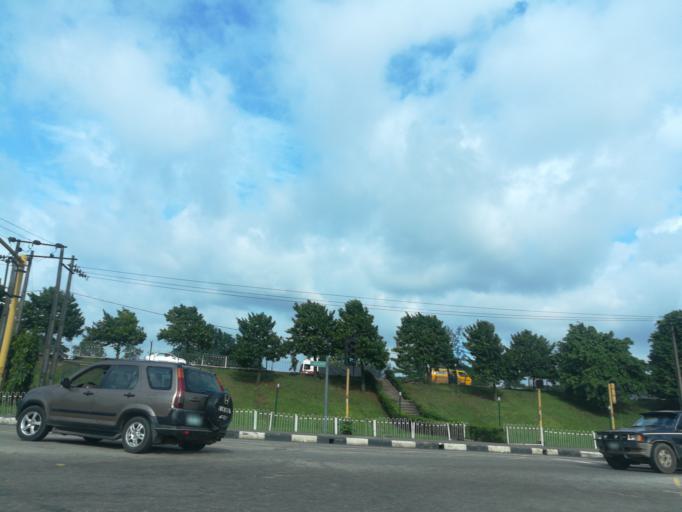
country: NG
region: Lagos
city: Ikeja
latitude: 6.6210
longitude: 3.3636
